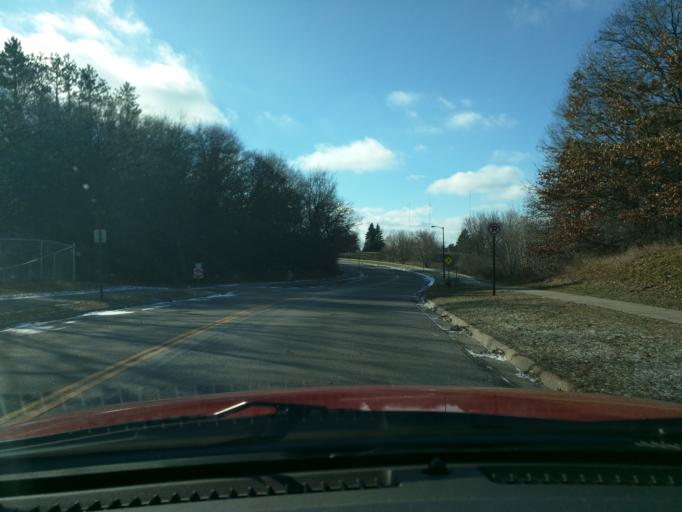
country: US
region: Minnesota
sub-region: Hennepin County
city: Eden Prairie
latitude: 44.8721
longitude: -93.4123
